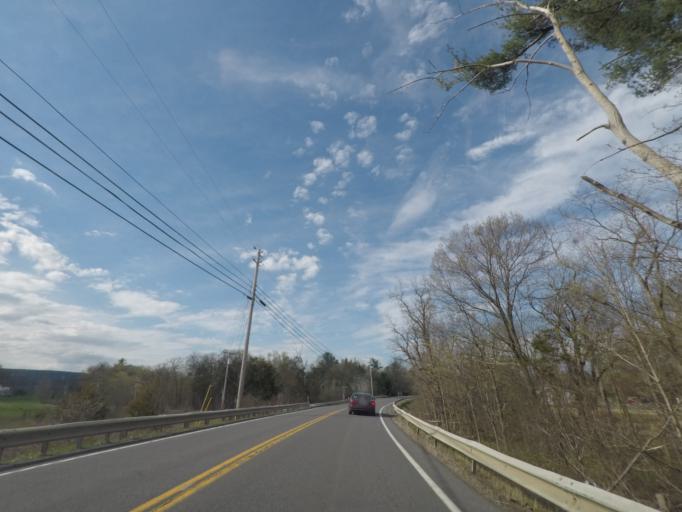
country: US
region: New York
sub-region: Albany County
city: Voorheesville
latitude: 42.5659
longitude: -73.9537
